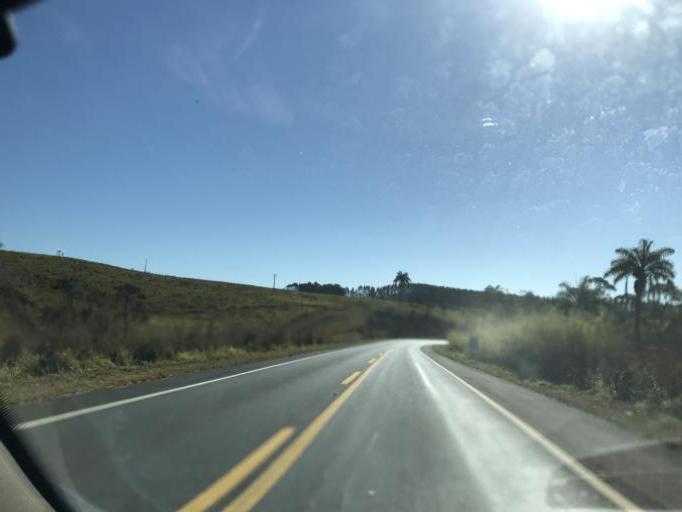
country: BR
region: Minas Gerais
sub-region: Bambui
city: Bambui
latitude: -19.8311
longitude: -46.0074
